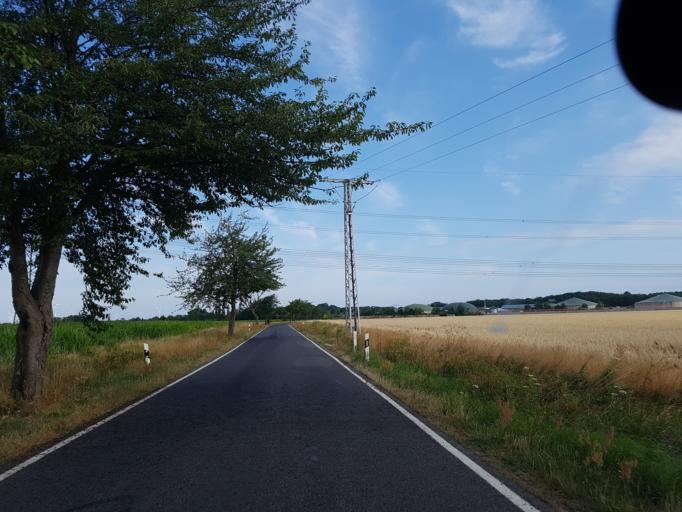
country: DE
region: Brandenburg
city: Drahnsdorf
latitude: 51.8469
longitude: 13.6253
